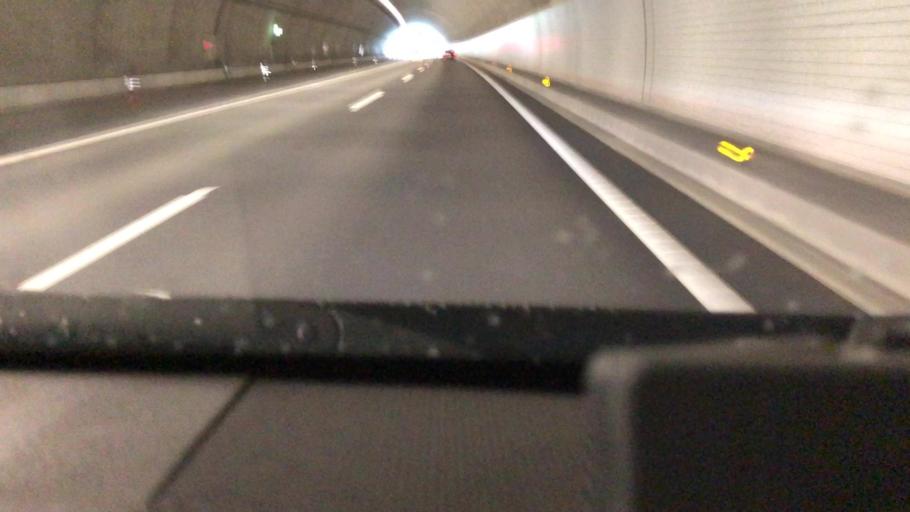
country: JP
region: Shizuoka
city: Kakegawa
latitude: 34.8417
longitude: 138.0245
